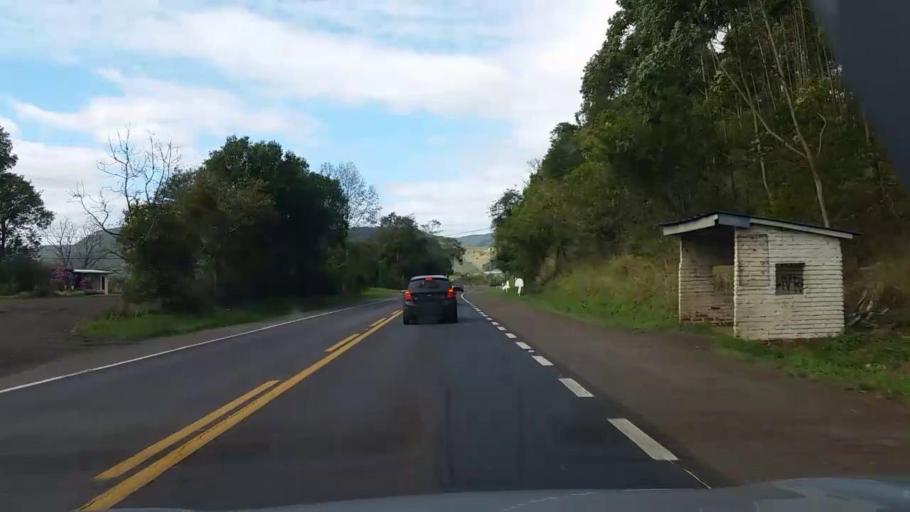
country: BR
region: Rio Grande do Sul
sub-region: Arroio Do Meio
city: Arroio do Meio
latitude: -29.3373
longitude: -52.0829
